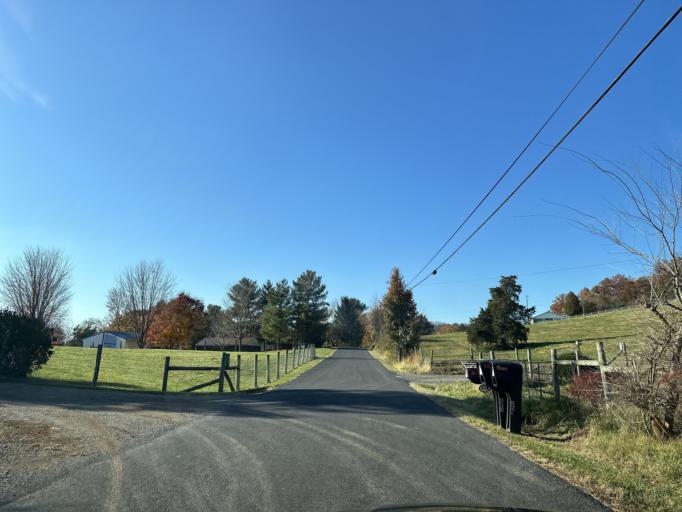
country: US
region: Virginia
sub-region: Augusta County
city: Weyers Cave
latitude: 38.2923
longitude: -78.9191
